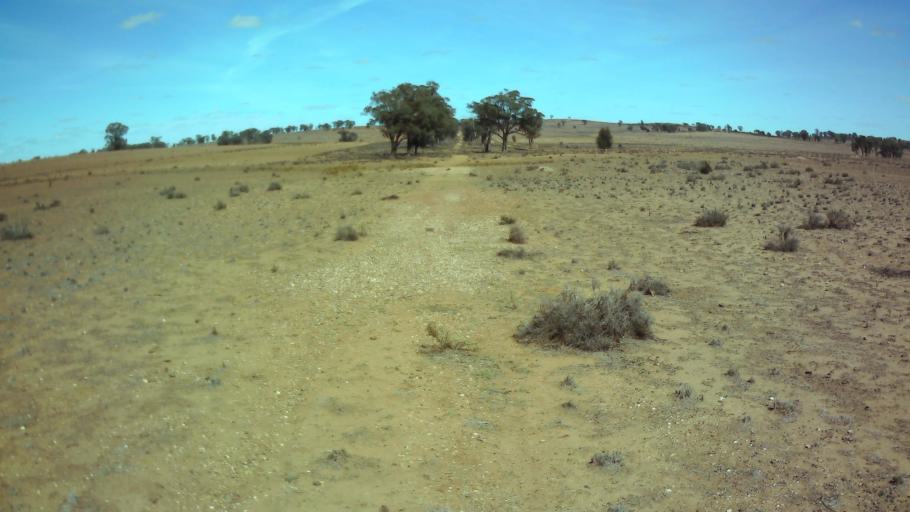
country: AU
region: New South Wales
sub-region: Weddin
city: Grenfell
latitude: -33.7223
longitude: 147.8516
